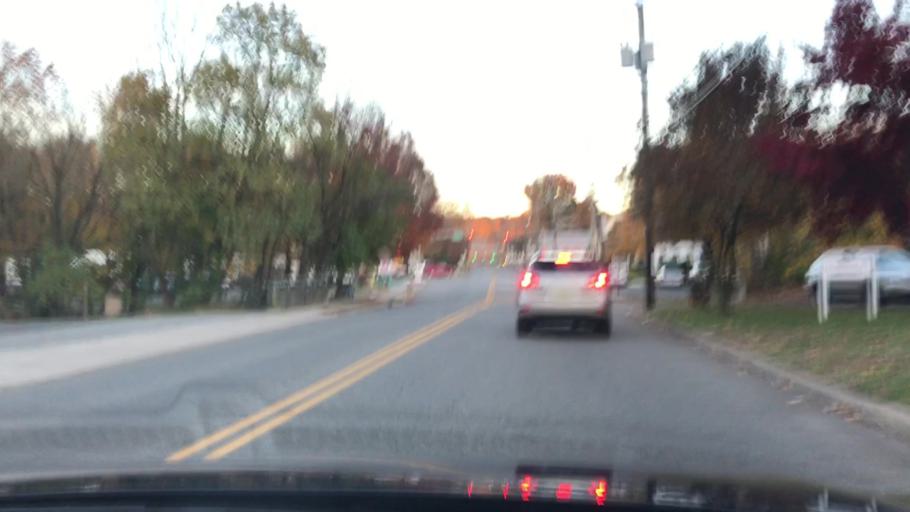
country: US
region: New Jersey
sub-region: Bergen County
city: Tenafly
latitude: 40.9248
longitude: -73.9693
